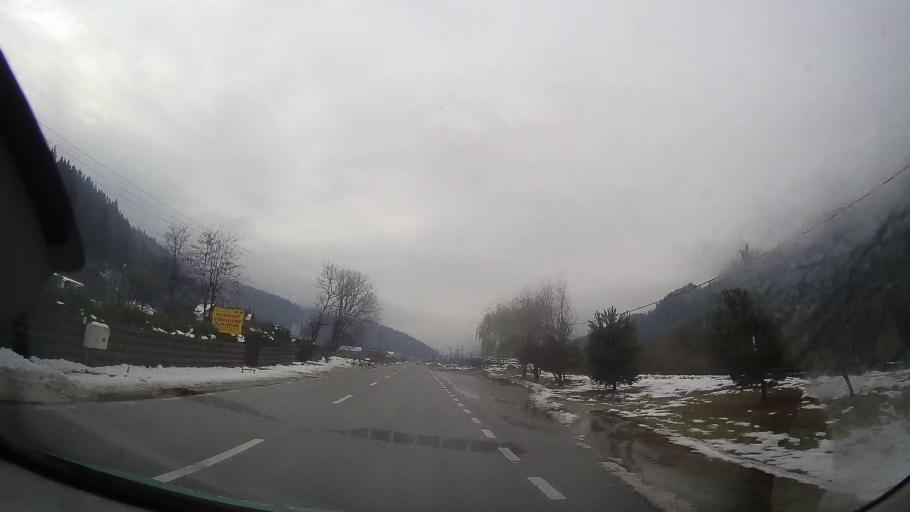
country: RO
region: Neamt
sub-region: Comuna Tasca
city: Tasca
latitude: 46.8828
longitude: 25.9980
